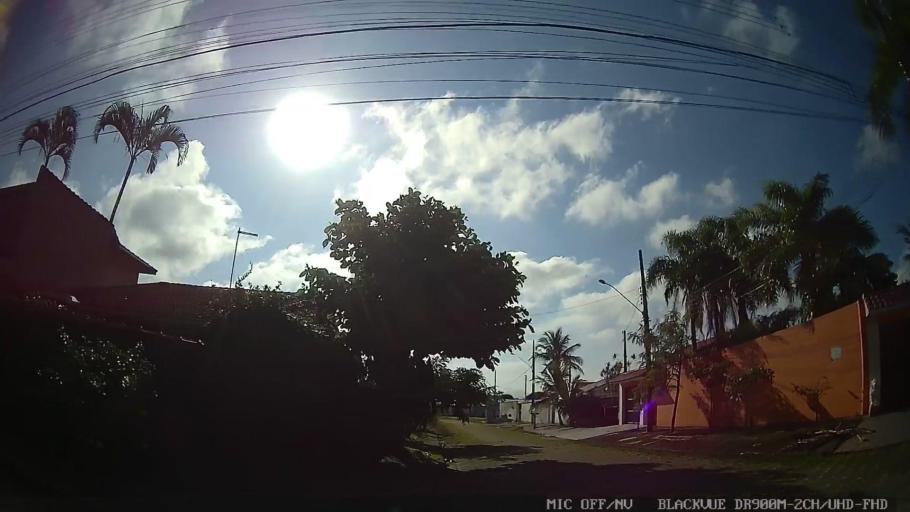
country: BR
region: Sao Paulo
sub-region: Peruibe
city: Peruibe
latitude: -24.2862
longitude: -46.9579
